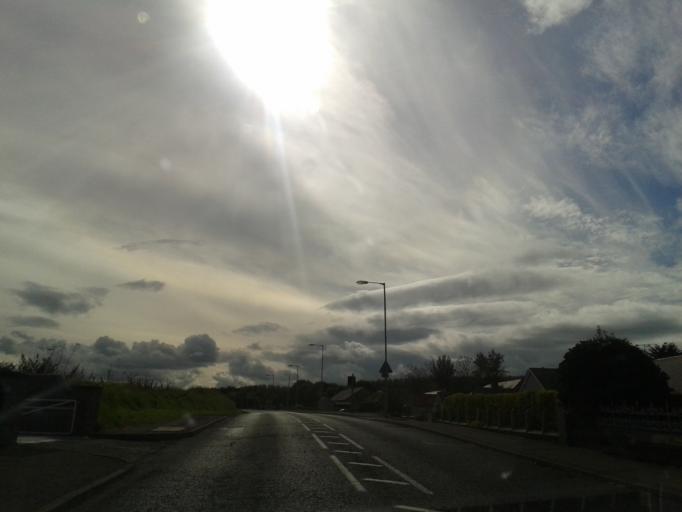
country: GB
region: Scotland
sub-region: Aberdeenshire
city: Portsoy
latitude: 57.6777
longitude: -2.6880
